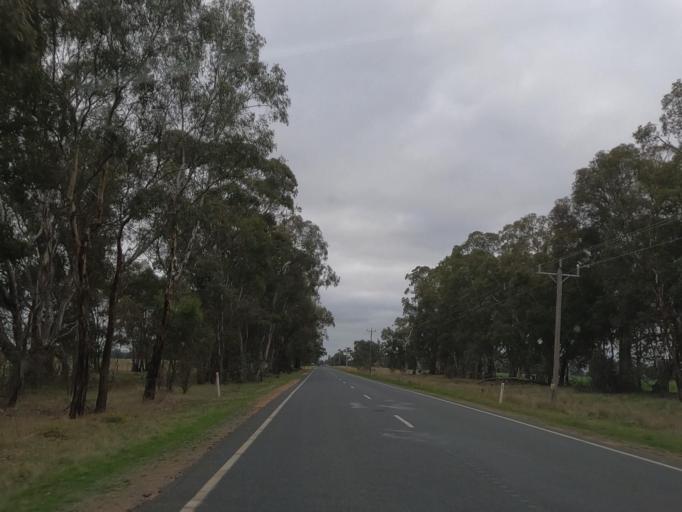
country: AU
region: Victoria
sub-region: Greater Bendigo
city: Long Gully
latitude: -36.4256
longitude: 143.9716
